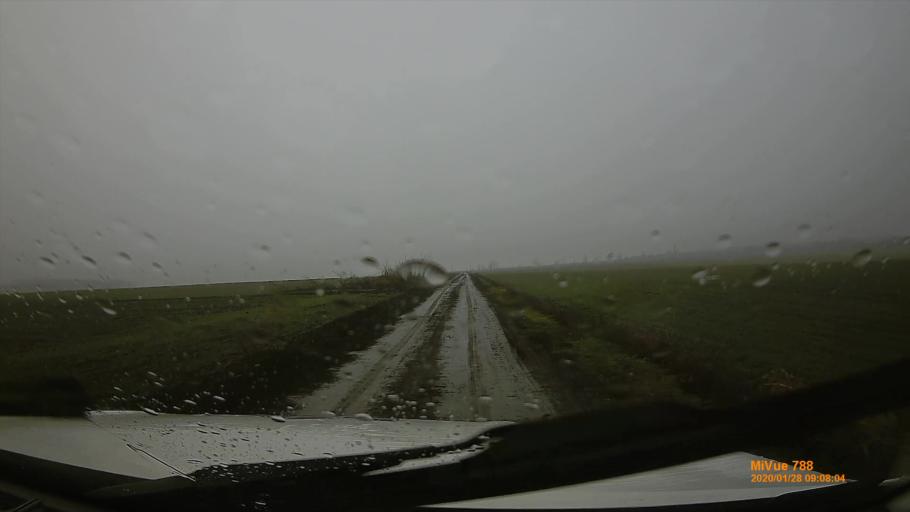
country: HU
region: Pest
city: Pilis
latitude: 47.3141
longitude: 19.5429
